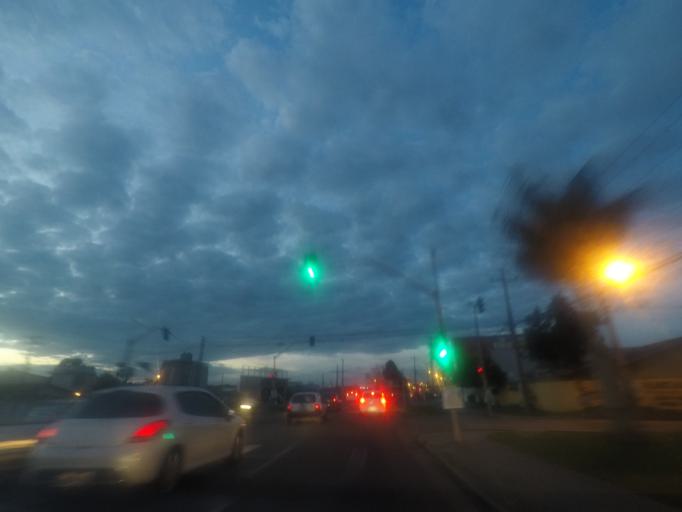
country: BR
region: Parana
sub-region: Pinhais
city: Pinhais
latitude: -25.4053
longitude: -49.1897
